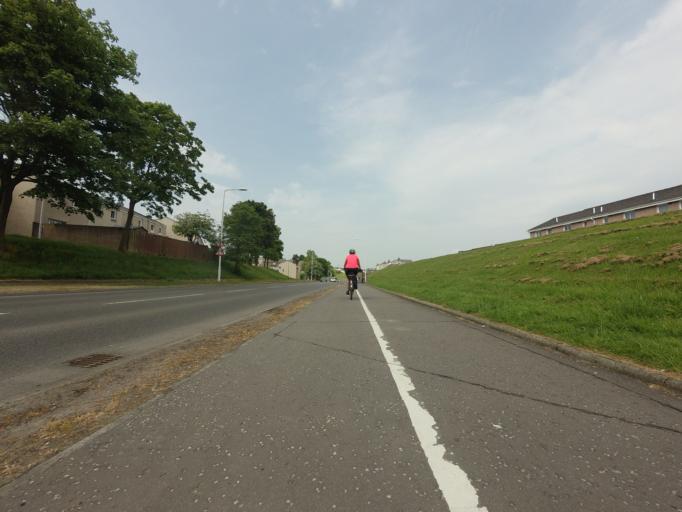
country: GB
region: Scotland
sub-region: Fife
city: Townhill
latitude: 56.0610
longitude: -3.4152
